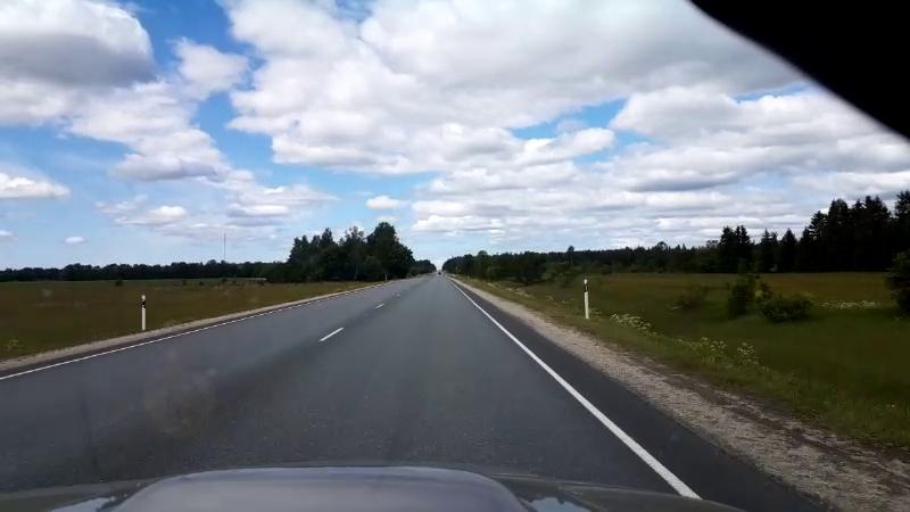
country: EE
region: Raplamaa
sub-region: Maerjamaa vald
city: Marjamaa
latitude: 58.9831
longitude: 24.4711
